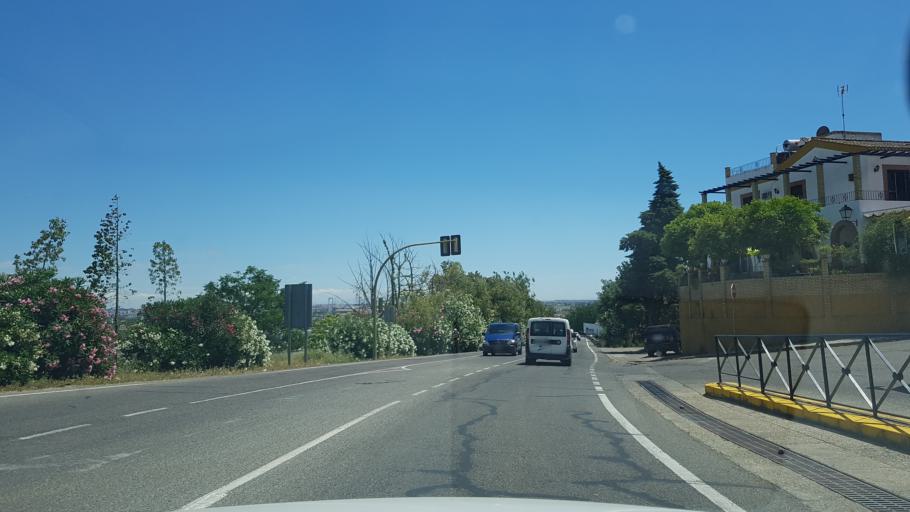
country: ES
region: Andalusia
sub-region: Provincia de Sevilla
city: Tomares
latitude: 37.3856
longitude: -6.0370
